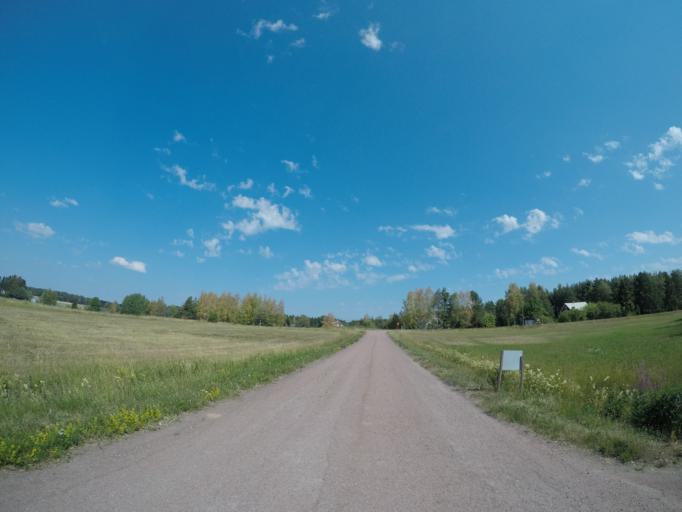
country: AX
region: Alands landsbygd
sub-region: Finstroem
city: Finstroem
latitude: 60.2101
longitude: 19.9042
